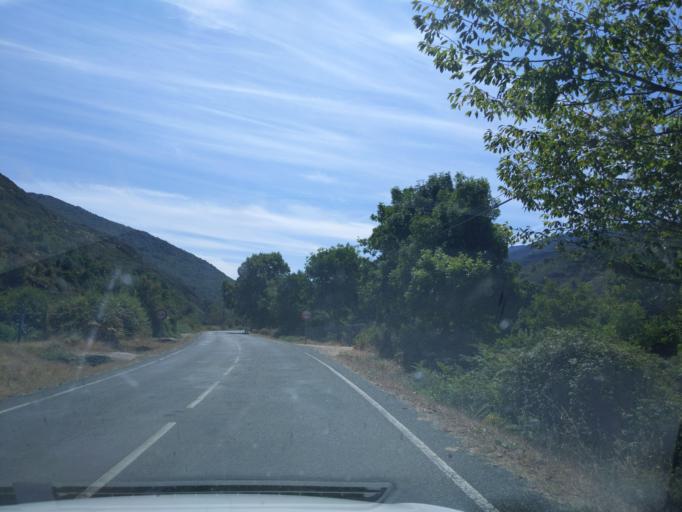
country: ES
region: La Rioja
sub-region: Provincia de La Rioja
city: Ezcaray
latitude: 42.2900
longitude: -3.0259
